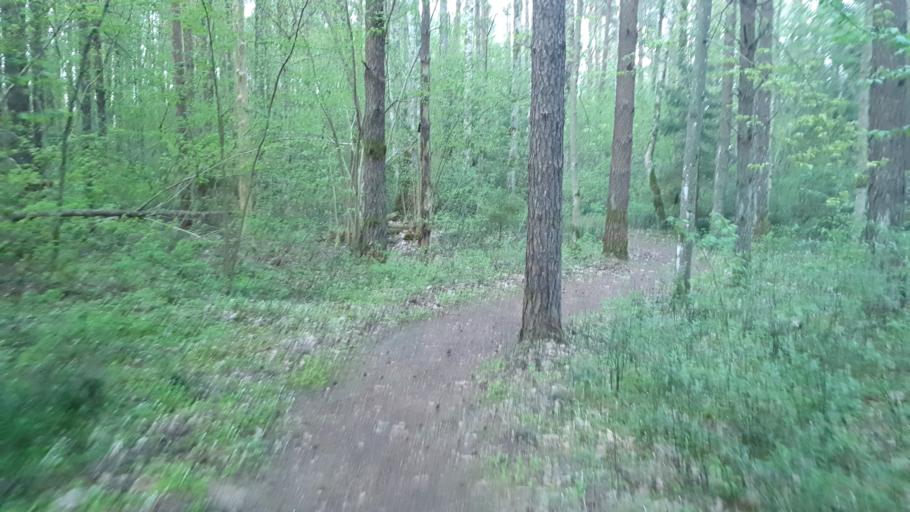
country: LV
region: Ikskile
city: Ikskile
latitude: 56.8354
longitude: 24.4389
